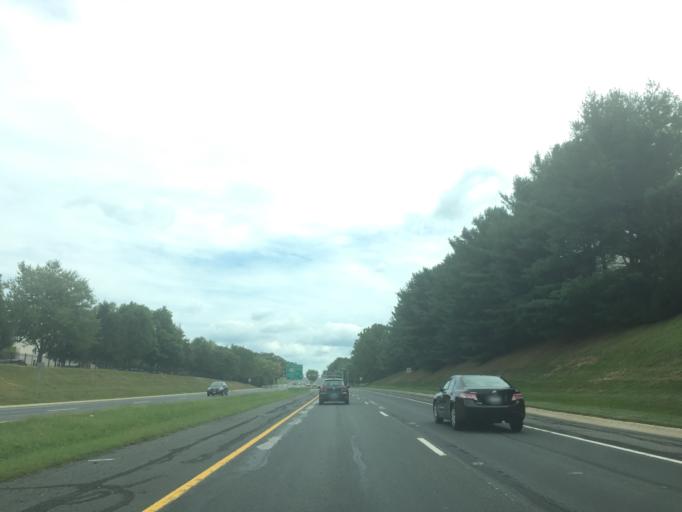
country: US
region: Maryland
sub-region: Montgomery County
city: Gaithersburg
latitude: 39.1528
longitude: -77.1778
